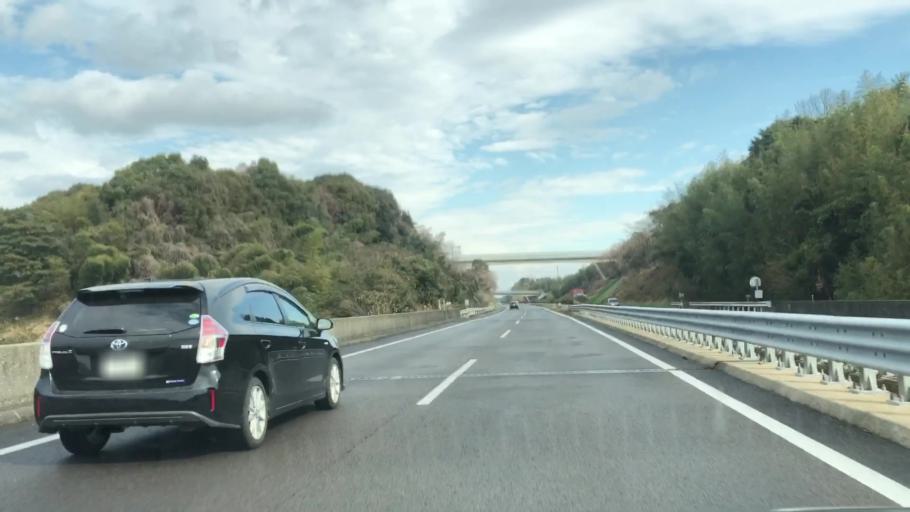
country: JP
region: Saga Prefecture
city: Tosu
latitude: 33.3677
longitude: 130.4585
